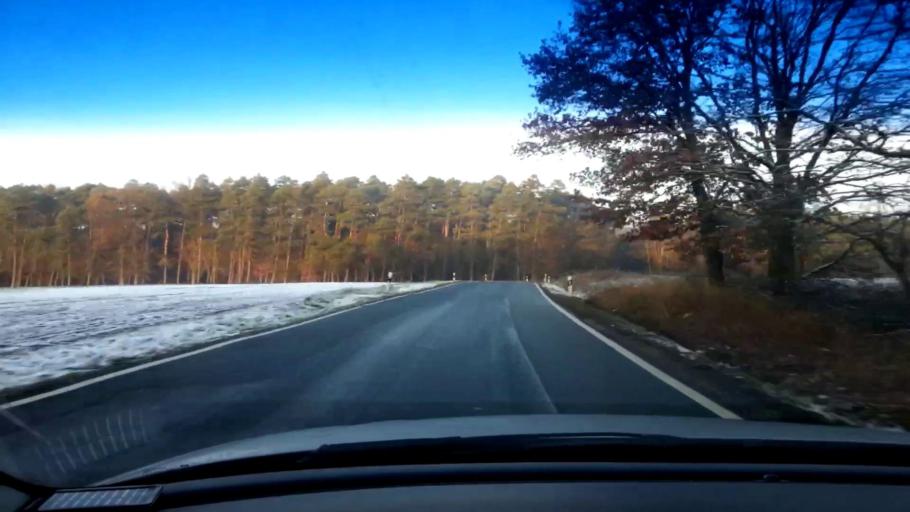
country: DE
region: Bavaria
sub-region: Upper Franconia
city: Pommersfelden
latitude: 49.7429
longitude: 10.8540
